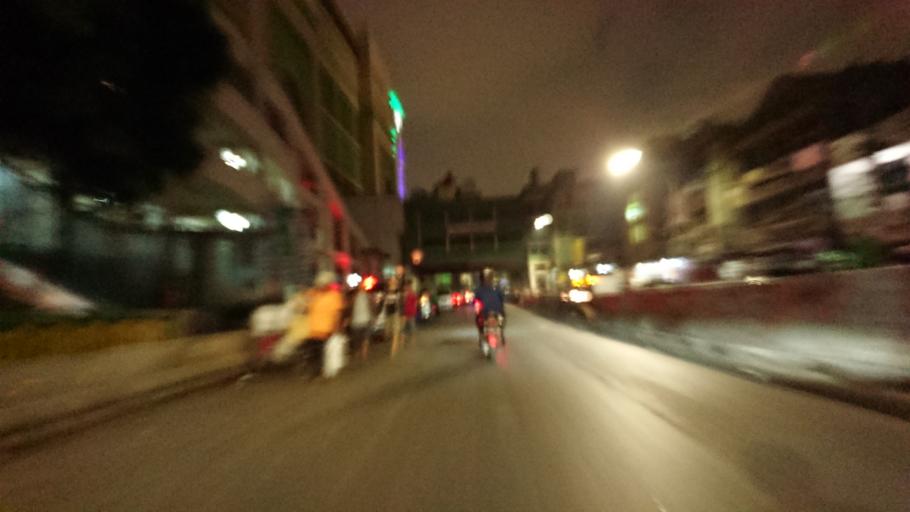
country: ID
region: Jakarta Raya
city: Jakarta
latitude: -6.1885
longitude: 106.8136
